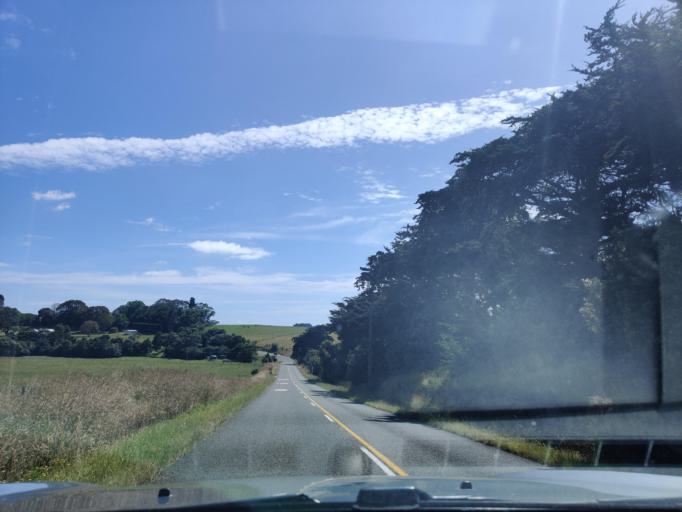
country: NZ
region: Manawatu-Wanganui
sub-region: Rangitikei District
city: Bulls
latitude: -40.1794
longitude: 175.4327
